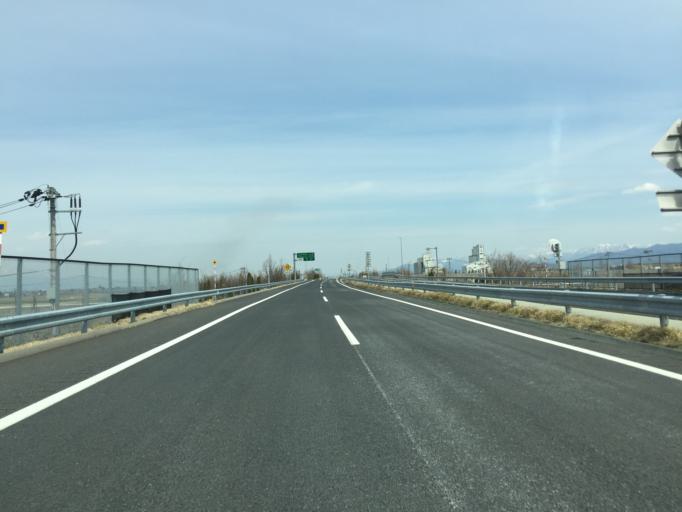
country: JP
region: Yamagata
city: Yamagata-shi
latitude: 38.2671
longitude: 140.2915
